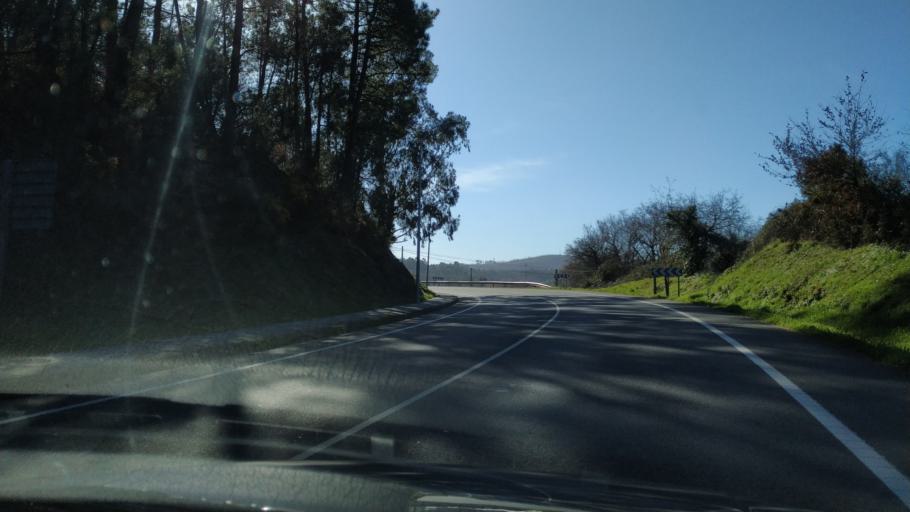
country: ES
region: Galicia
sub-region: Provincia de Pontevedra
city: Silleda
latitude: 42.7032
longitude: -8.2588
